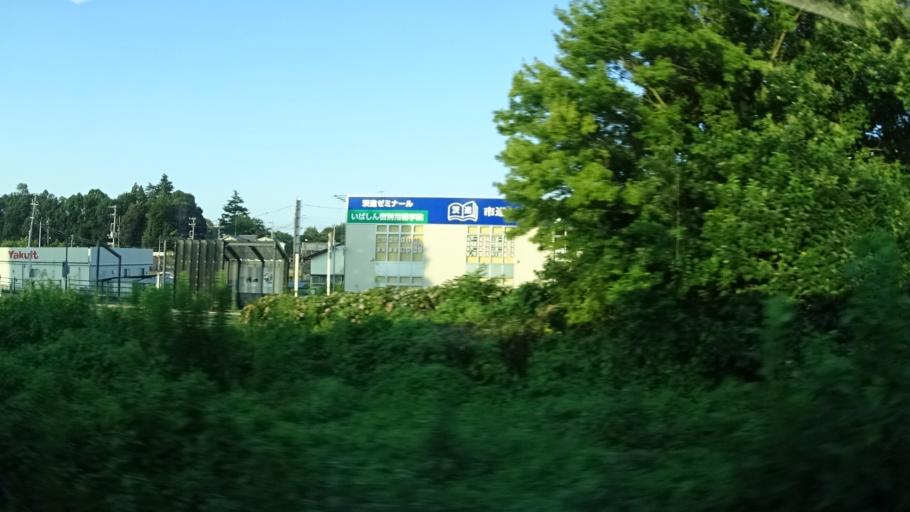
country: JP
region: Ibaraki
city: Ishioka
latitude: 36.1886
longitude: 140.2816
